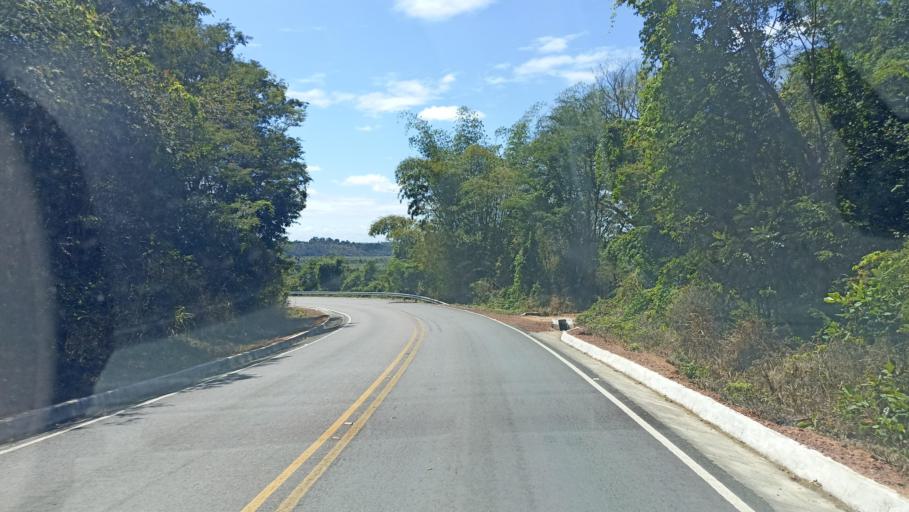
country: BR
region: Bahia
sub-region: Andarai
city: Vera Cruz
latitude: -12.7656
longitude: -41.3259
